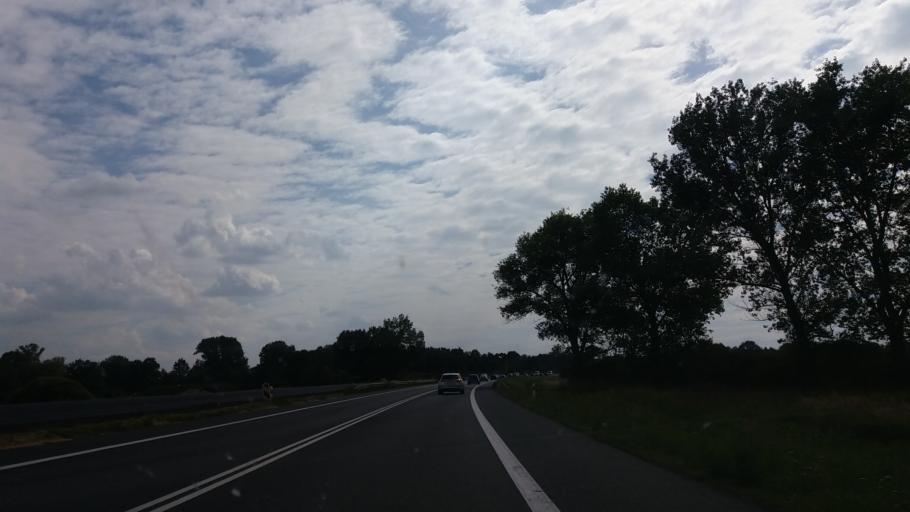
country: PL
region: Lubusz
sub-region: Powiat zielonogorski
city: Sulechow
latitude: 52.0209
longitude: 15.6293
